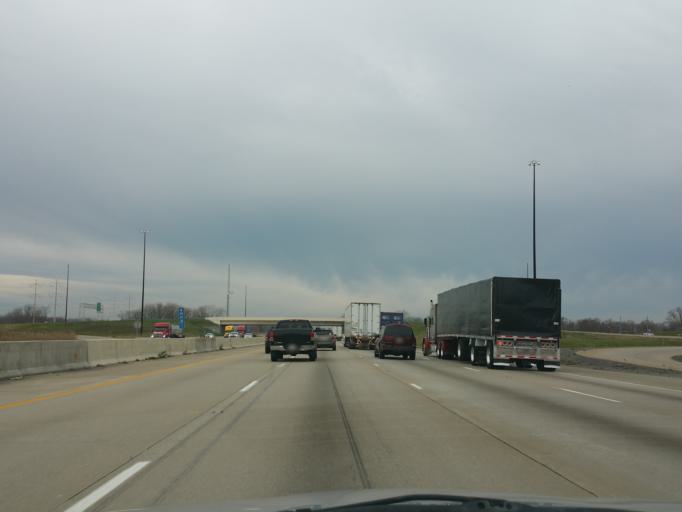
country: US
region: Indiana
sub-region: Lake County
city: Gary
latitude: 41.5675
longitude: -87.3321
